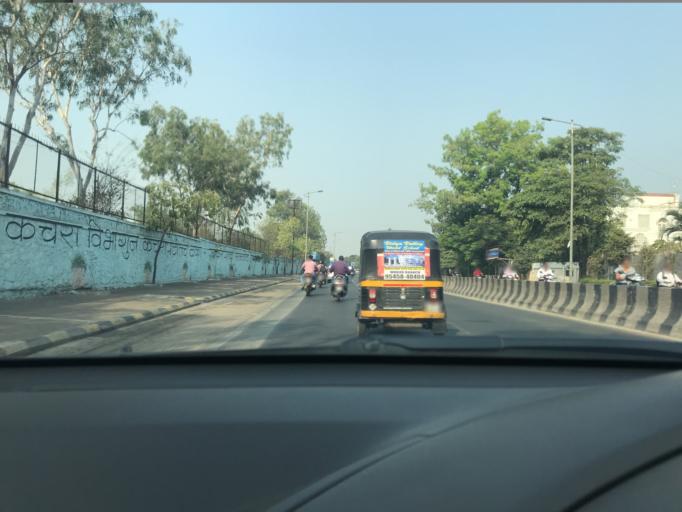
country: IN
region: Maharashtra
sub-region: Pune Division
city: Khadki
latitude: 18.5490
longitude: 73.8122
